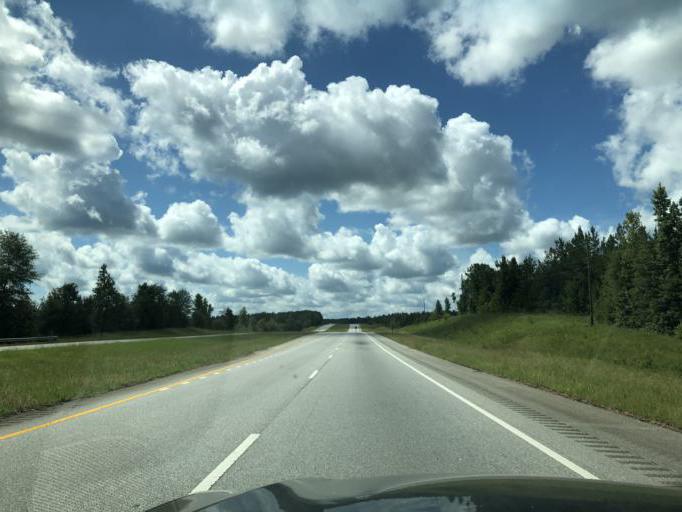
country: US
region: Alabama
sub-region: Russell County
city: Ladonia
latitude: 32.2312
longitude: -85.1710
